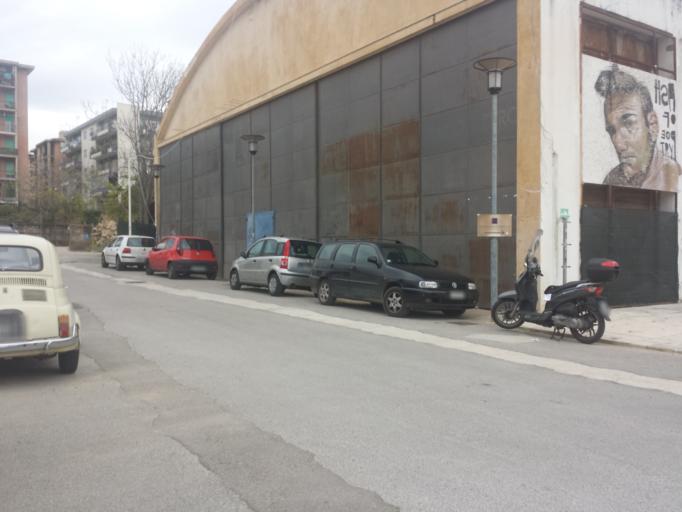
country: IT
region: Sicily
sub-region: Palermo
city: Palermo
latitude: 38.1178
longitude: 13.3386
